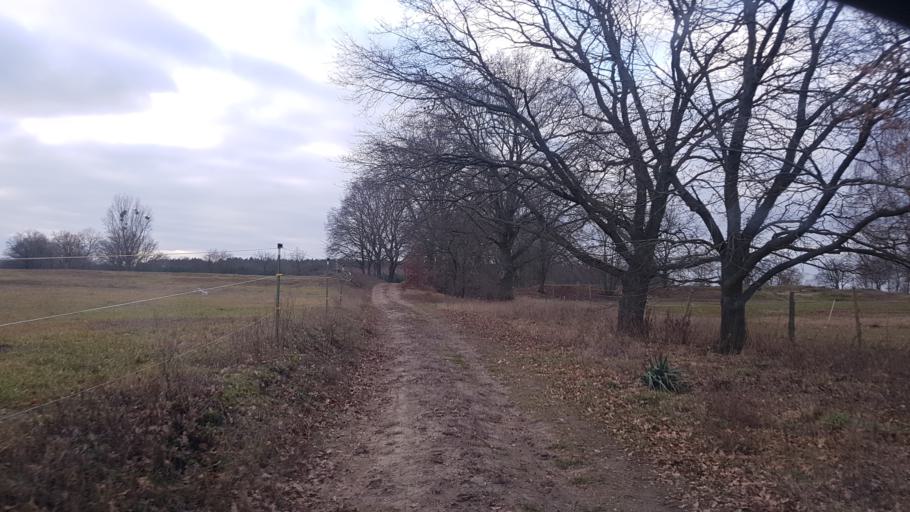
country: DE
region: Brandenburg
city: Ludwigsfelde
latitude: 52.3325
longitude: 13.2212
